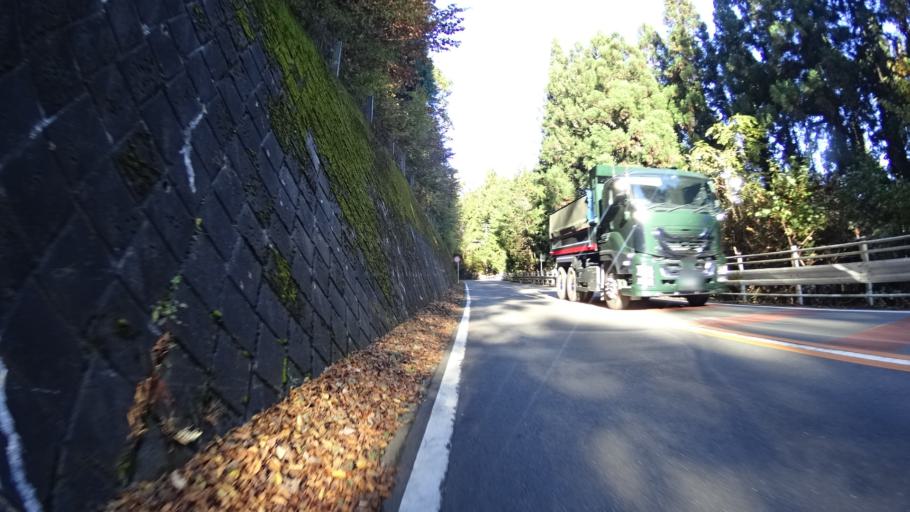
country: JP
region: Yamanashi
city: Uenohara
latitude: 35.6999
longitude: 139.1031
